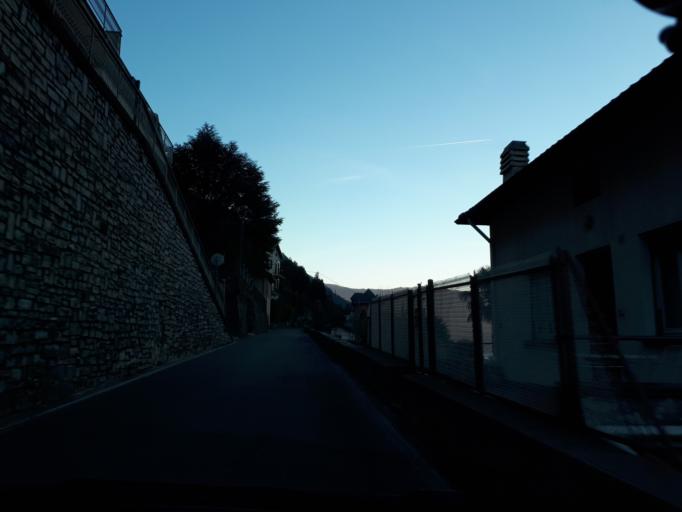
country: IT
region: Lombardy
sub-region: Provincia di Como
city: Nesso
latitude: 45.9165
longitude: 9.1537
